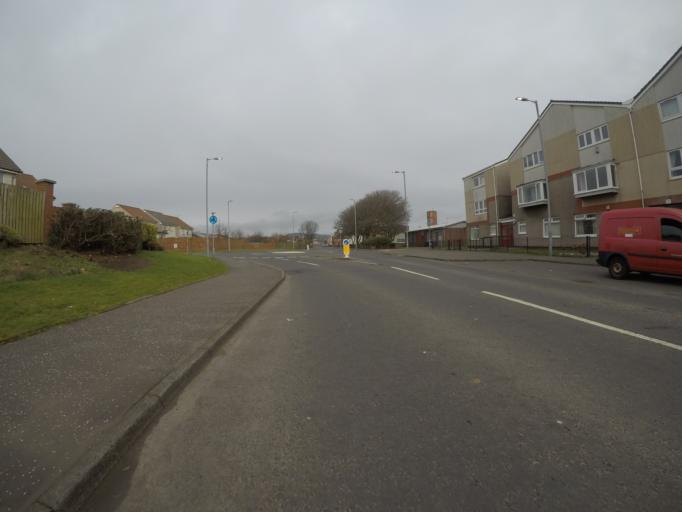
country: GB
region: Scotland
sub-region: North Ayrshire
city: Ardrossan
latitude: 55.6425
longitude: -4.8149
